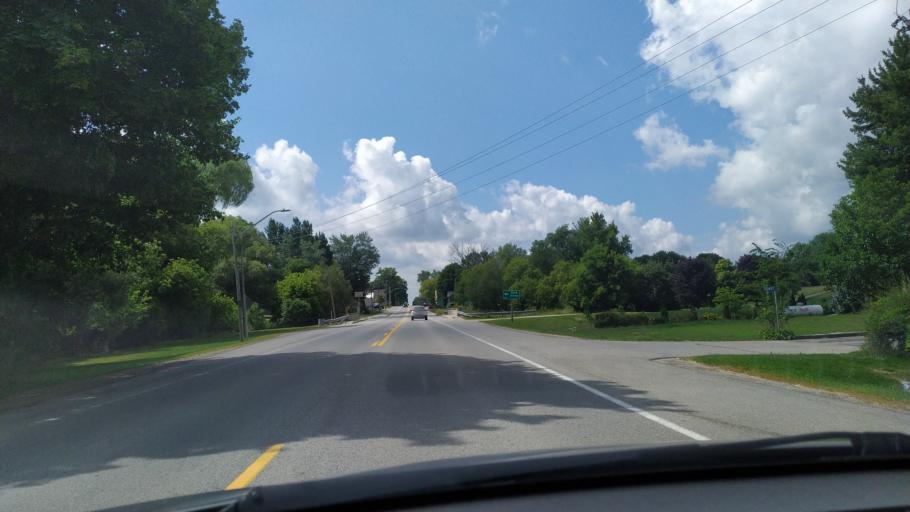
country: CA
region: Ontario
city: South Huron
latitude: 43.3266
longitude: -81.3114
